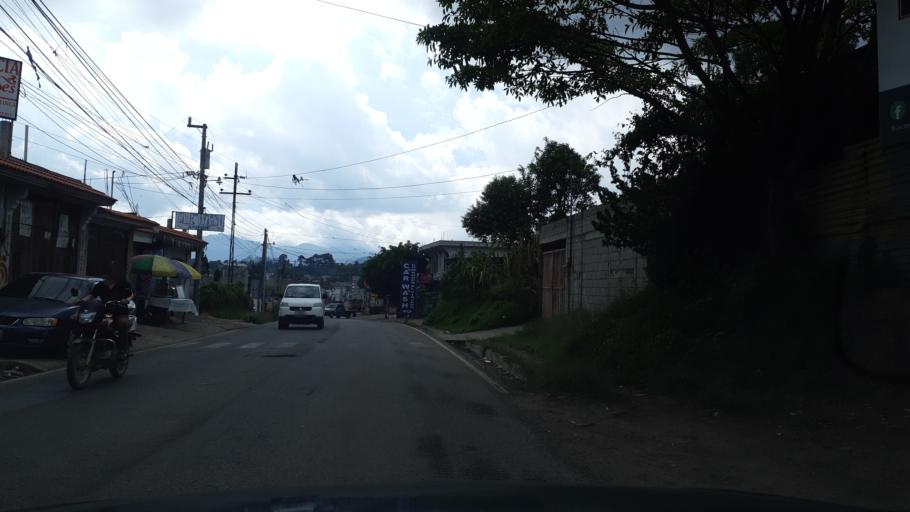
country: GT
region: Chimaltenango
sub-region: Municipio de Chimaltenango
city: Chimaltenango
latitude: 14.6731
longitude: -90.8053
